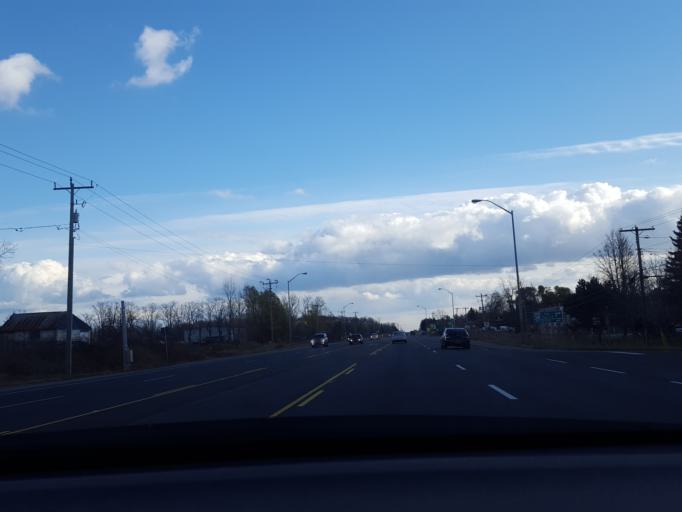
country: CA
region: Ontario
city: Ancaster
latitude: 43.3390
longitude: -79.9545
